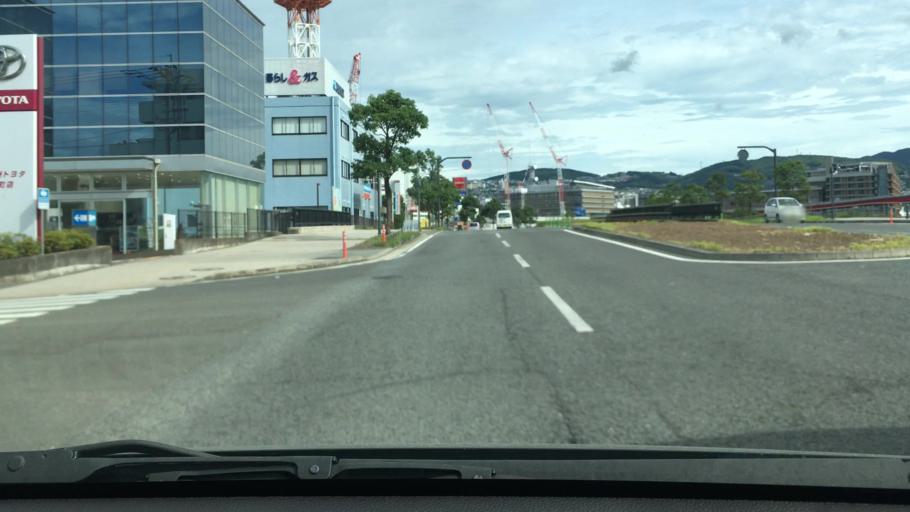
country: JP
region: Nagasaki
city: Nagasaki-shi
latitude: 32.7561
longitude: 129.8660
